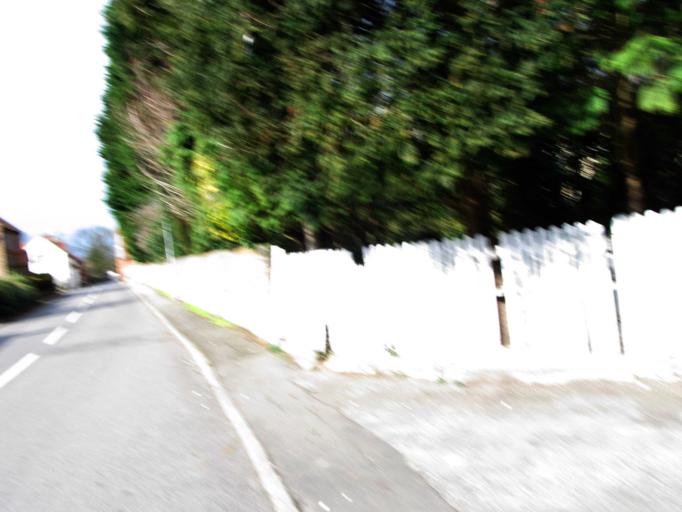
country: GB
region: England
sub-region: Nottinghamshire
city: Retford
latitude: 53.3878
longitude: -0.9099
